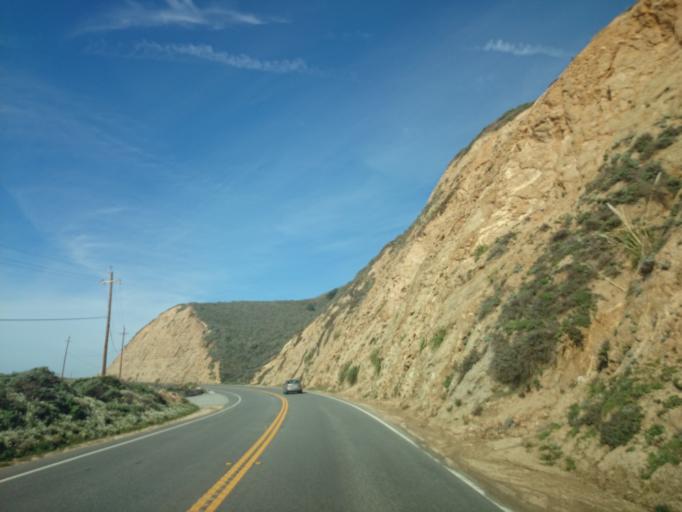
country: US
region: California
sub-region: San Mateo County
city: Montara
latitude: 37.5559
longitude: -122.5128
